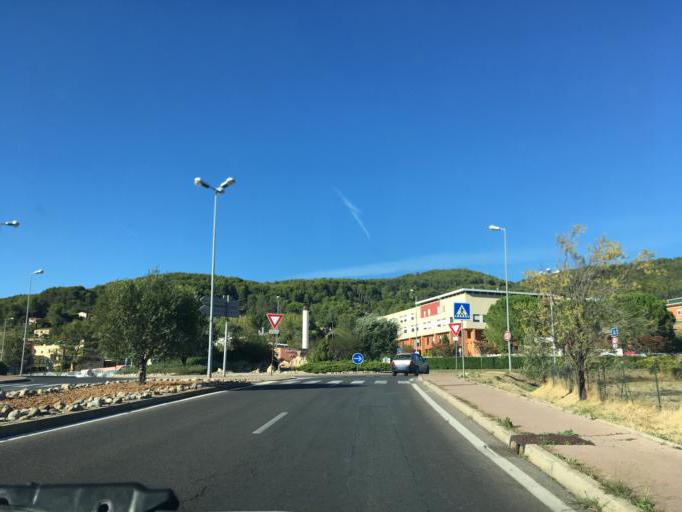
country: FR
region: Provence-Alpes-Cote d'Azur
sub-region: Departement du Var
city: Draguignan
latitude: 43.5477
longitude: 6.4446
